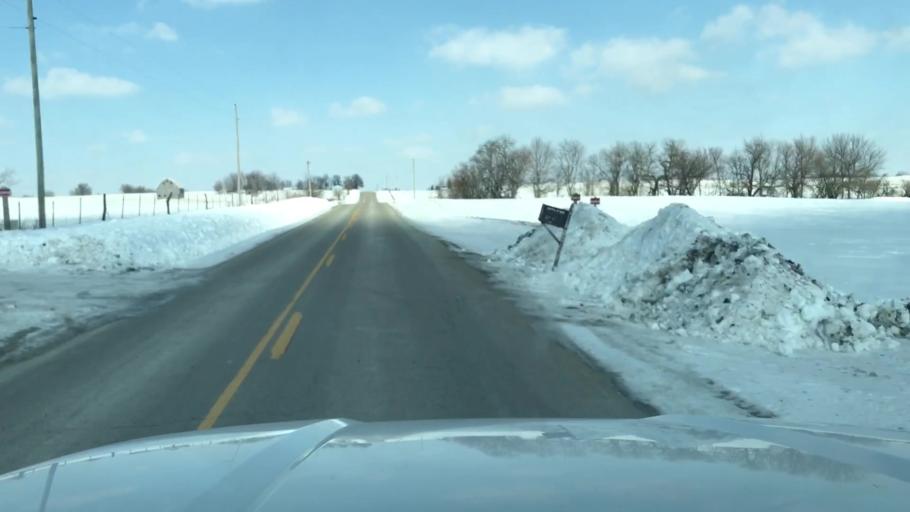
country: US
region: Missouri
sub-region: Nodaway County
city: Maryville
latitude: 40.3497
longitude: -94.7223
